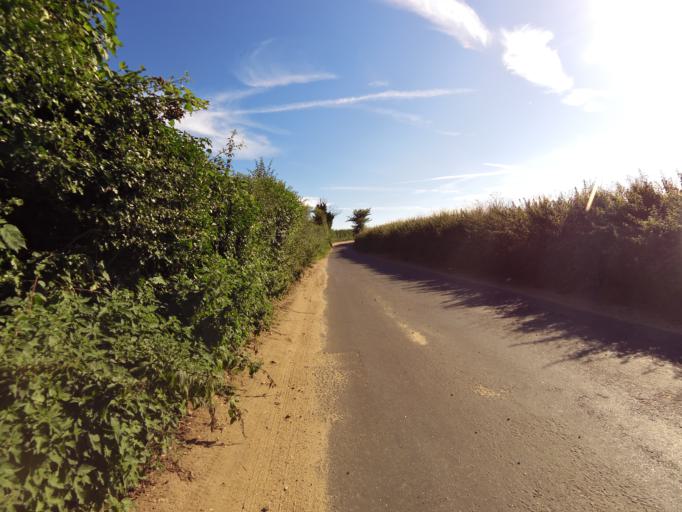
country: GB
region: England
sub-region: Suffolk
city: Kesgrave
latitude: 52.0318
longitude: 1.2642
